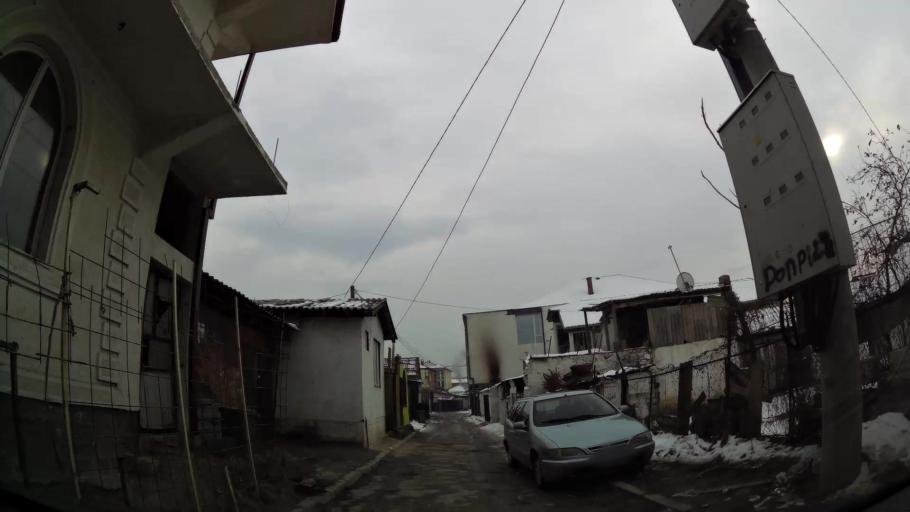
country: MK
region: Suto Orizari
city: Suto Orizare
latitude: 42.0448
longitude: 21.4223
